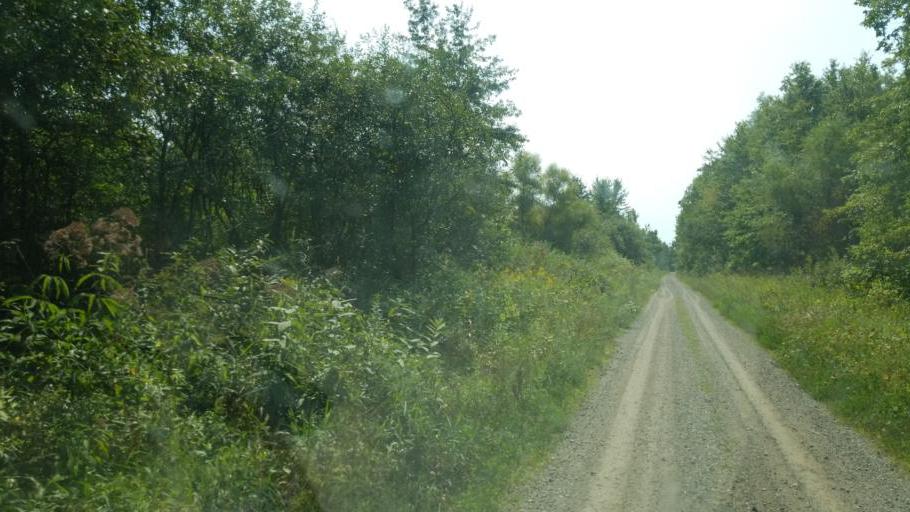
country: US
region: Ohio
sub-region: Ashtabula County
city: Orwell
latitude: 41.4797
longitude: -80.9047
